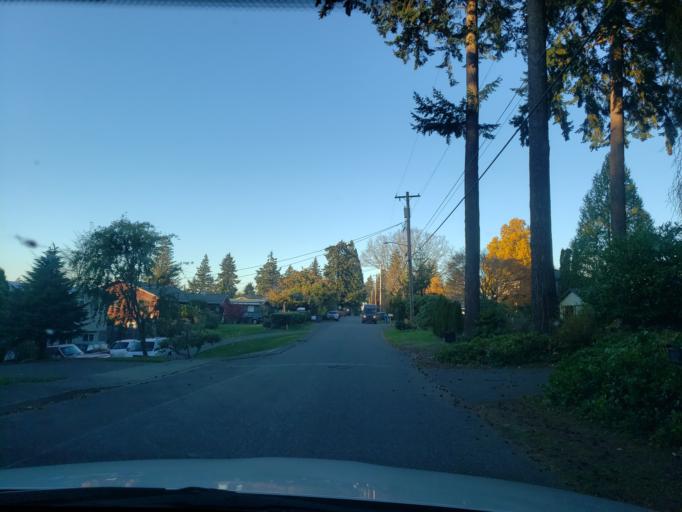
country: US
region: Washington
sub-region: Snohomish County
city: Esperance
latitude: 47.7942
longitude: -122.3642
